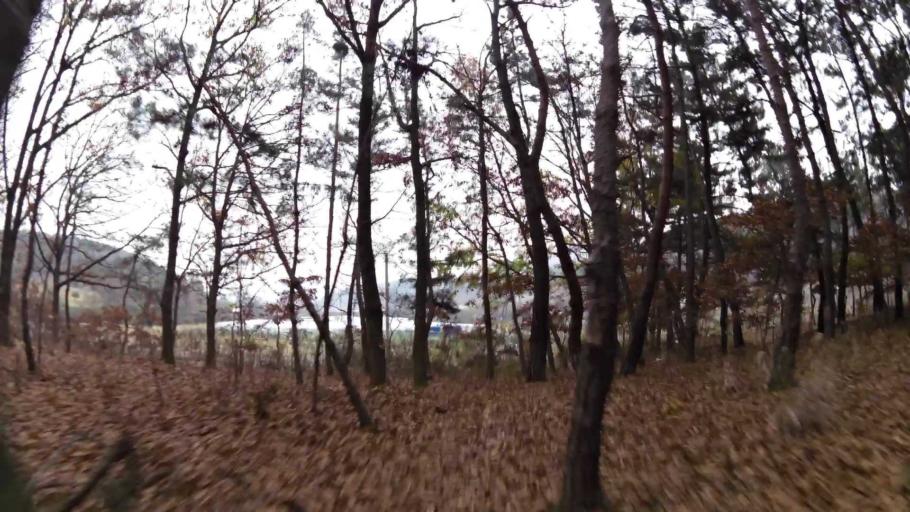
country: KR
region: Daegu
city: Daegu
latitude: 35.8598
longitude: 128.6684
